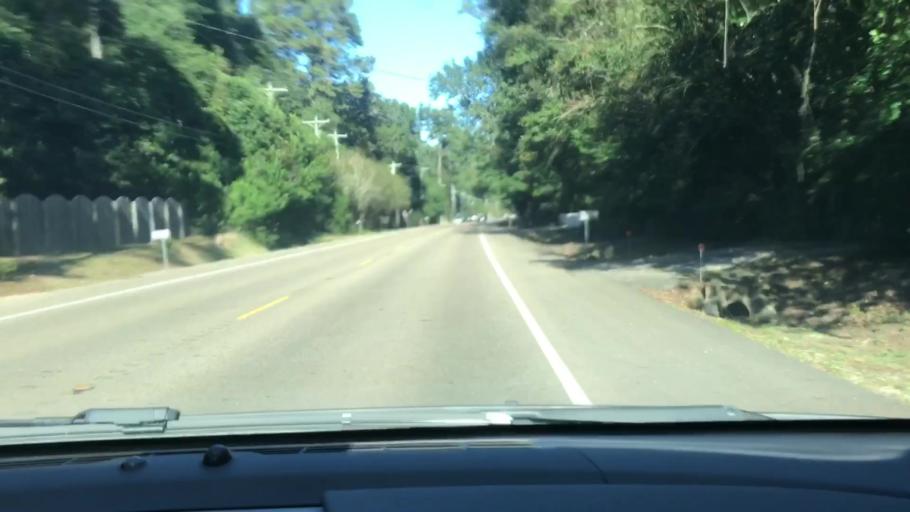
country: US
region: Louisiana
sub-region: Saint Tammany Parish
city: Abita Springs
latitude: 30.4934
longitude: -90.0700
